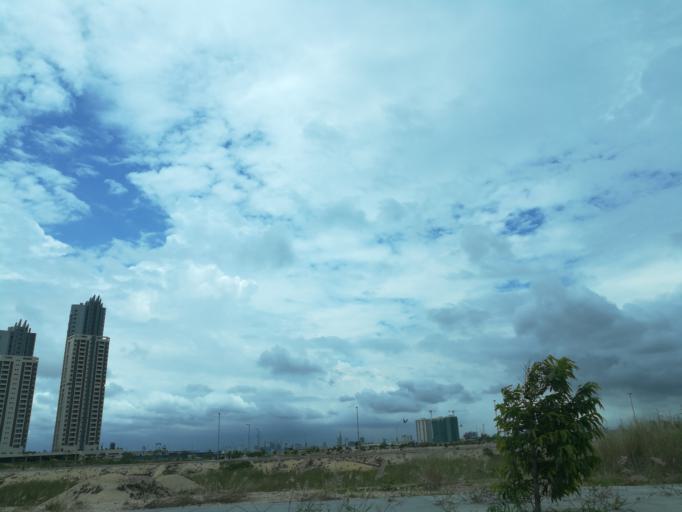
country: NG
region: Lagos
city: Ikoyi
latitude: 6.4062
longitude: 3.4139
